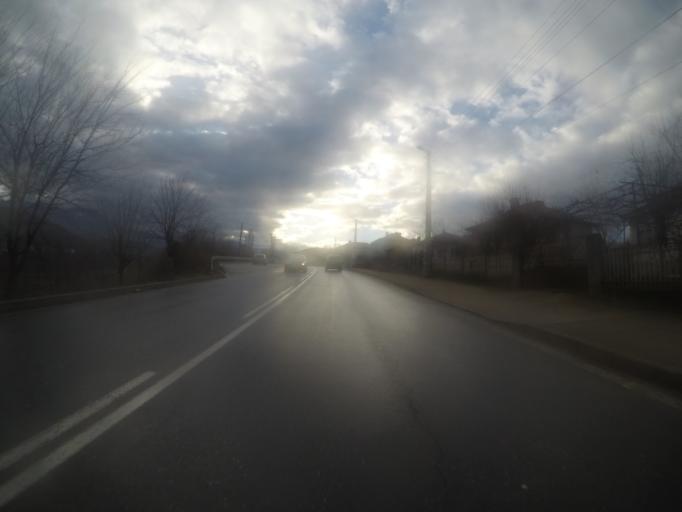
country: BG
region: Blagoevgrad
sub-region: Obshtina Simitli
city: Simitli
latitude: 41.8851
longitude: 23.1196
